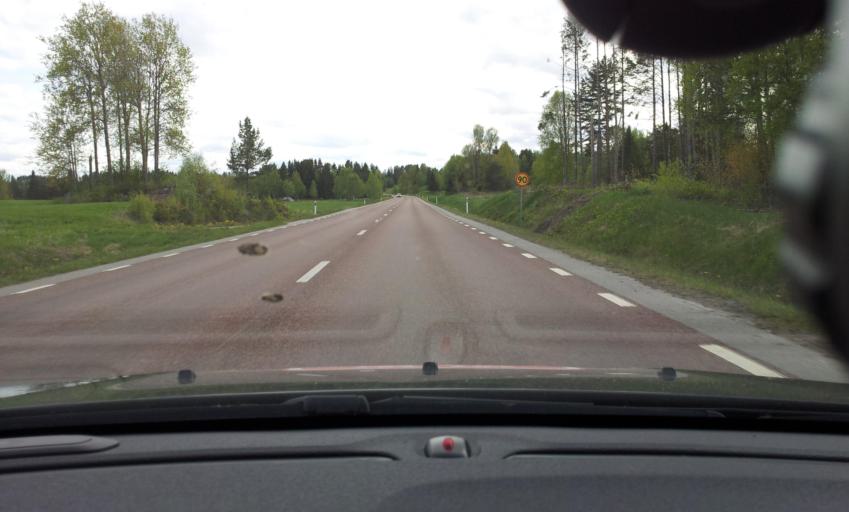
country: SE
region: Jaemtland
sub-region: Bergs Kommun
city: Hoverberg
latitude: 62.9685
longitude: 14.5577
